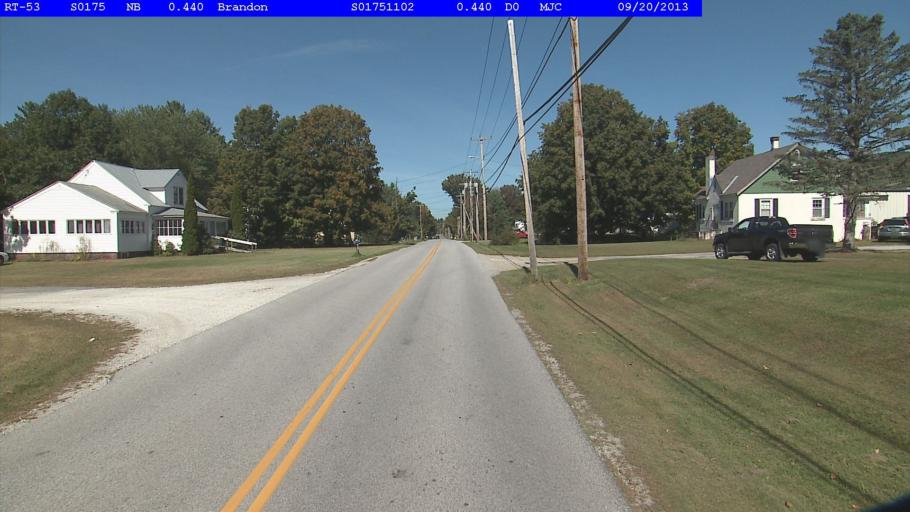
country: US
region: Vermont
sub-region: Rutland County
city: Brandon
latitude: 43.8331
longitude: -73.0554
